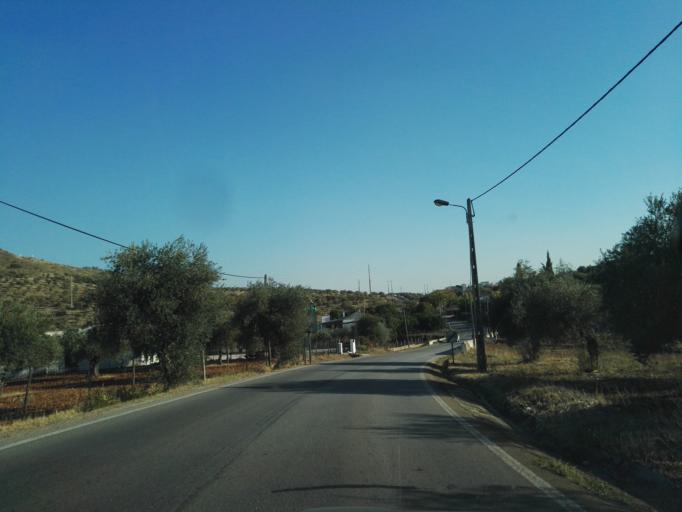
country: PT
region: Portalegre
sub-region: Elvas
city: Elvas
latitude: 38.8956
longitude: -7.1734
